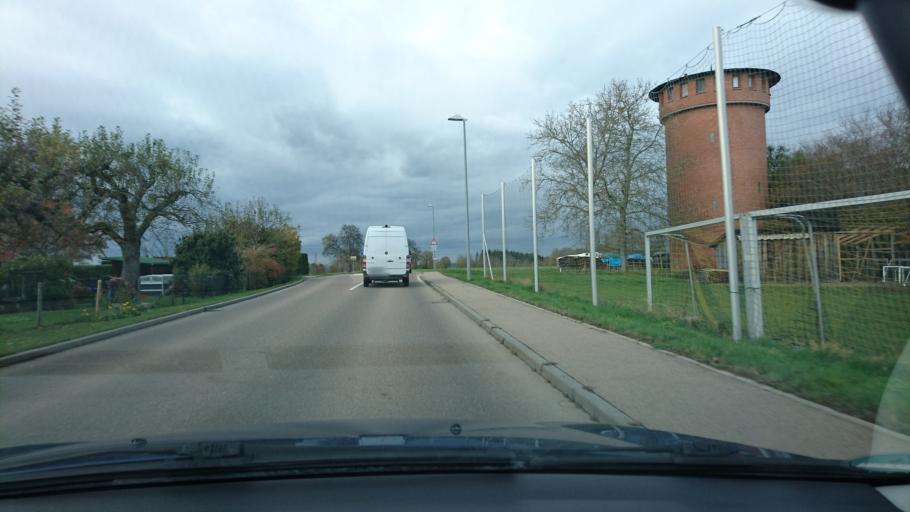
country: DE
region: Baden-Wuerttemberg
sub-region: Regierungsbezirk Stuttgart
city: Gschwend
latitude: 48.9311
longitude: 9.7943
